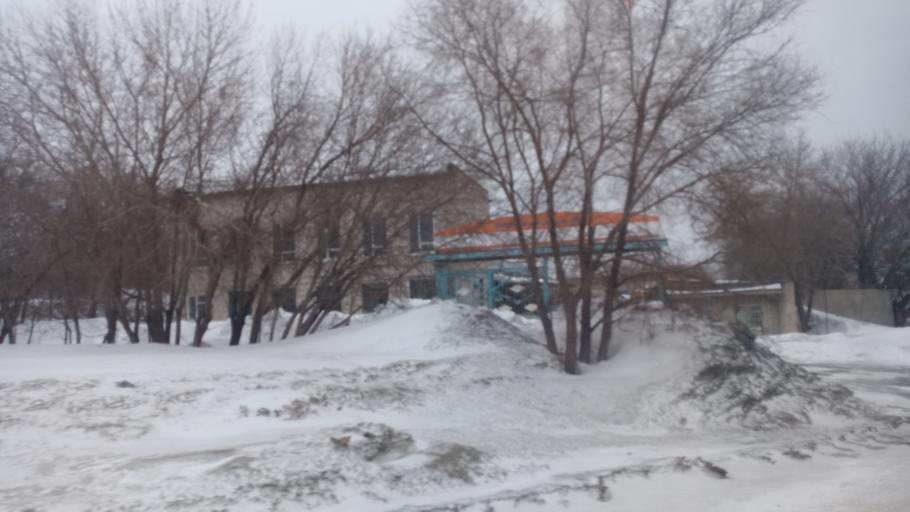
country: RU
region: Altai Krai
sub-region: Gorod Barnaulskiy
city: Barnaul
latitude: 53.3898
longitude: 83.6771
